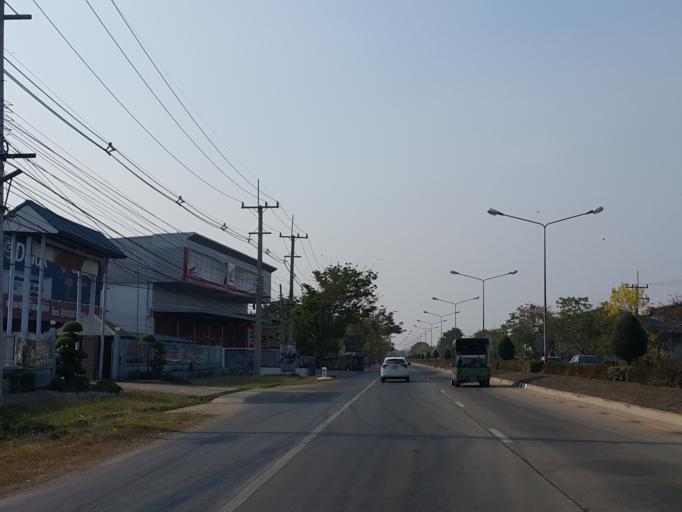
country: TH
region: Suphan Buri
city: Sam Chuk
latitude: 14.7583
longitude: 100.0957
